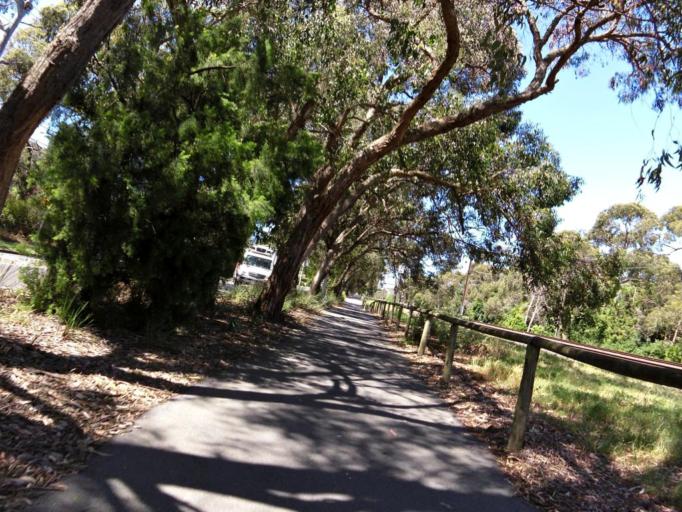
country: AU
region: Victoria
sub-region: Knox
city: Ferntree Gully
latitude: -37.8750
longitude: 145.2920
